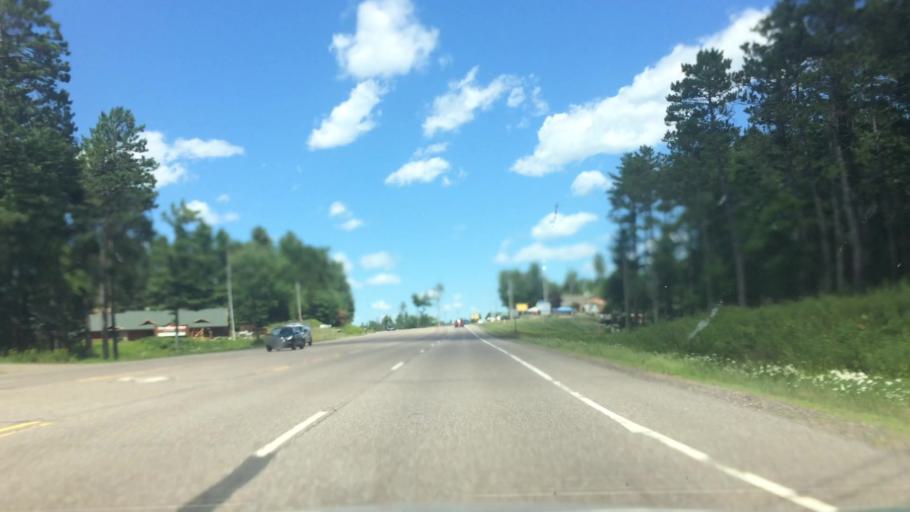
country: US
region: Wisconsin
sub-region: Vilas County
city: Lac du Flambeau
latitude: 45.8487
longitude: -89.7039
